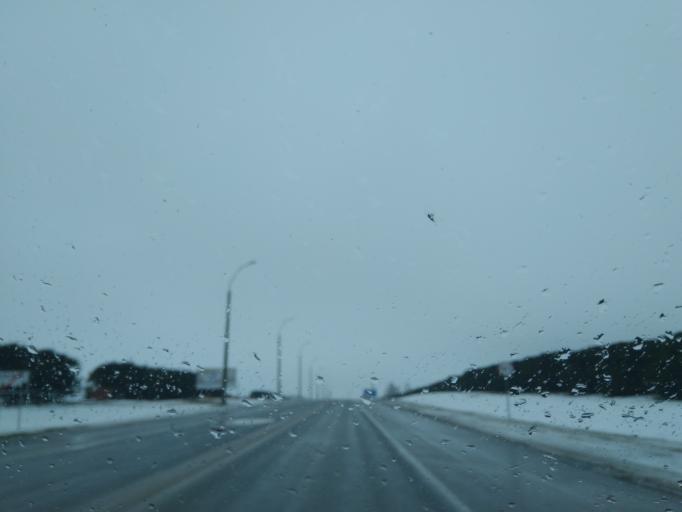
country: BY
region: Minsk
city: Nyasvizh
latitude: 53.2364
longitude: 26.6401
